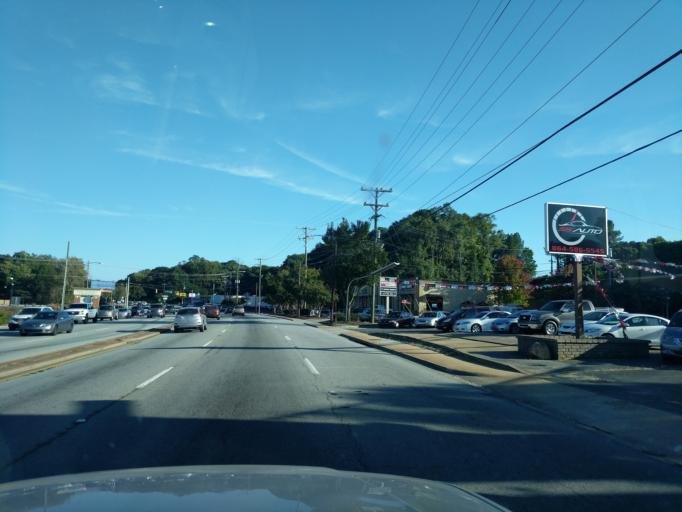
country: US
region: South Carolina
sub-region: Spartanburg County
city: Spartanburg
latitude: 34.9665
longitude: -81.9326
